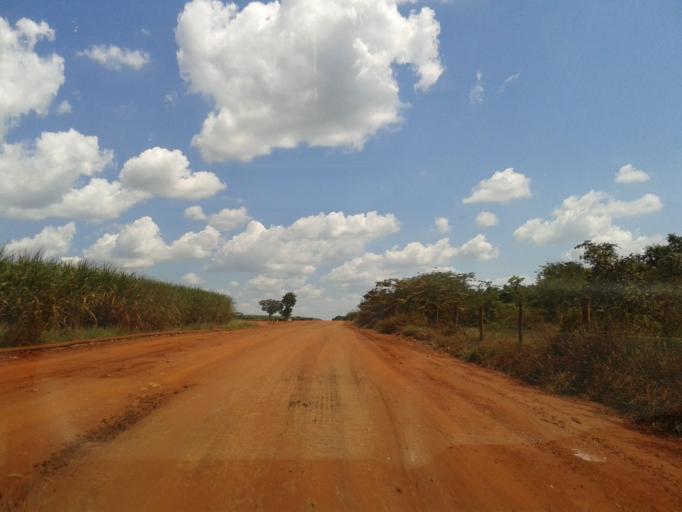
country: BR
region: Minas Gerais
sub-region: Ituiutaba
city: Ituiutaba
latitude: -19.0417
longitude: -49.7062
